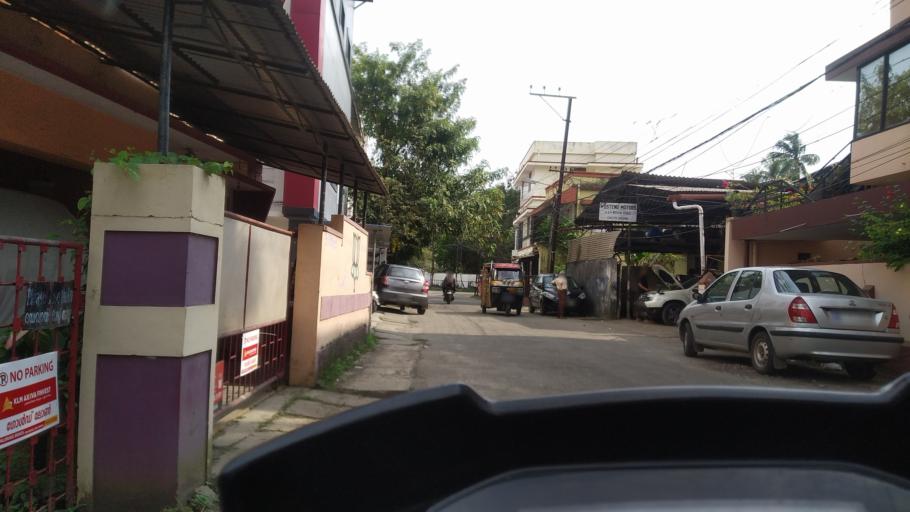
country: IN
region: Kerala
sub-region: Ernakulam
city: Cochin
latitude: 9.9627
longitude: 76.2921
